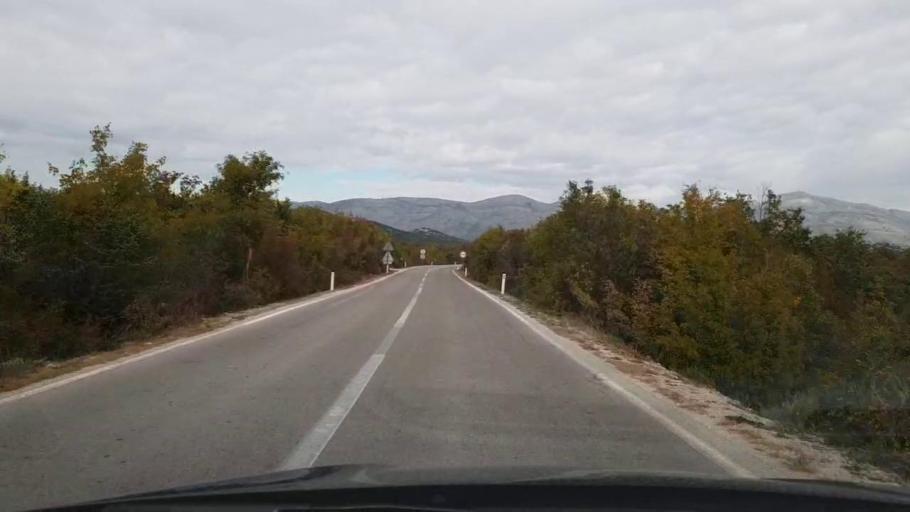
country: HR
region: Dubrovacko-Neretvanska
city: Cibaca
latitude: 42.6720
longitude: 18.2310
